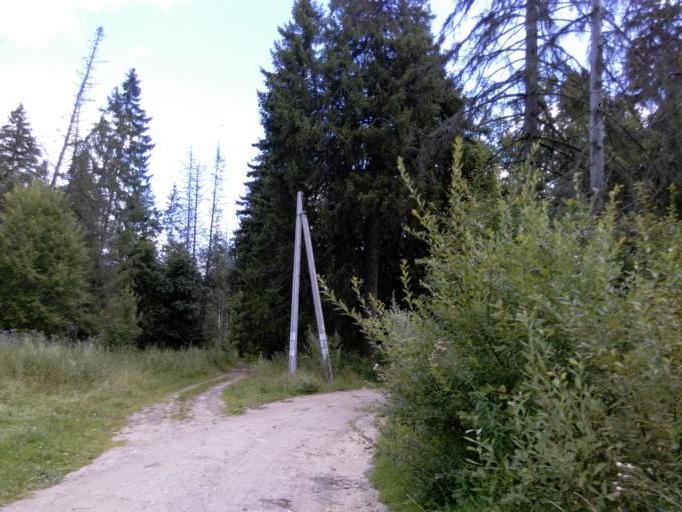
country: RU
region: Moskovskaya
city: Solnechnogorsk
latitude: 56.1364
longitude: 36.9057
